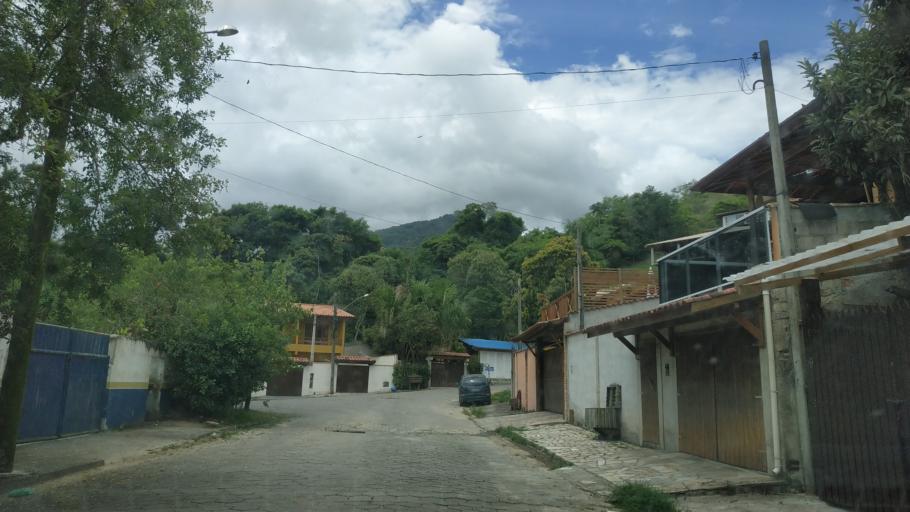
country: BR
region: Sao Paulo
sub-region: Ilhabela
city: Ilhabela
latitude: -23.8252
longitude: -45.3572
